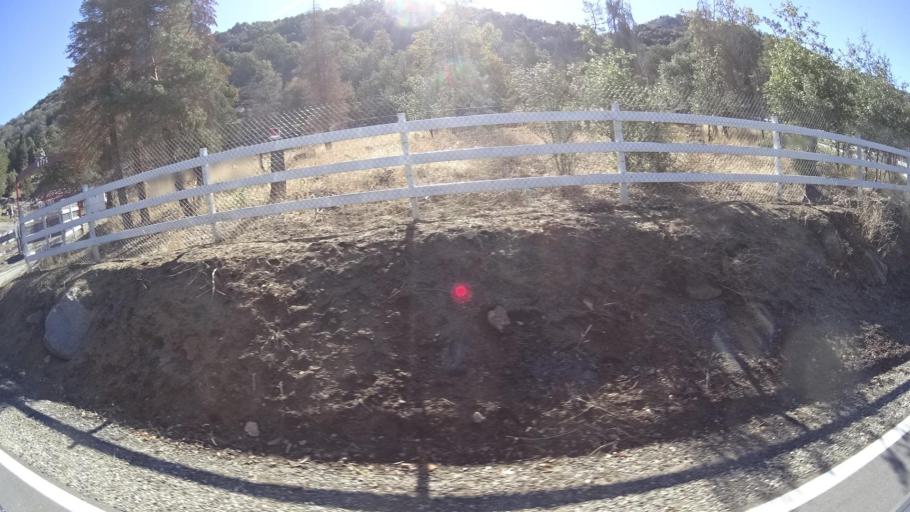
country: US
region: California
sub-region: Kern County
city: Alta Sierra
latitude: 35.7356
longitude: -118.6596
